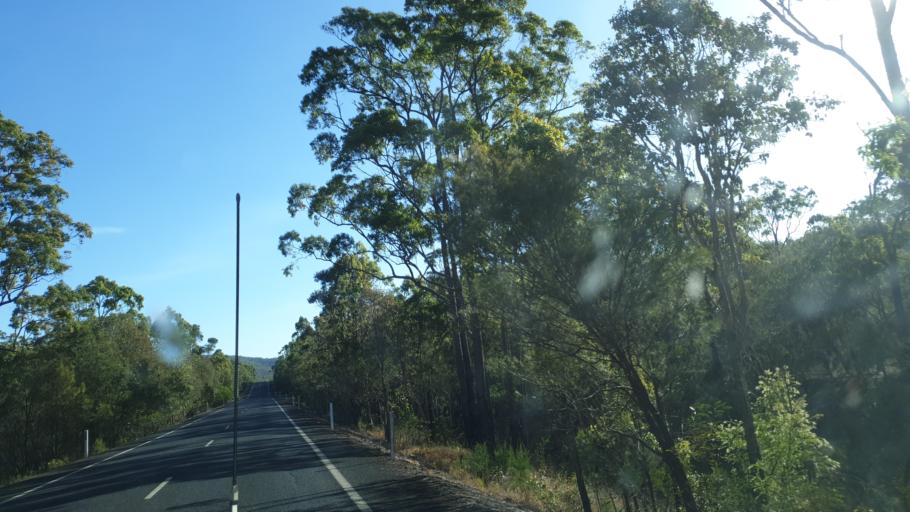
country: AU
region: Queensland
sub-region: Tablelands
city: Atherton
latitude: -17.3519
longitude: 145.4117
